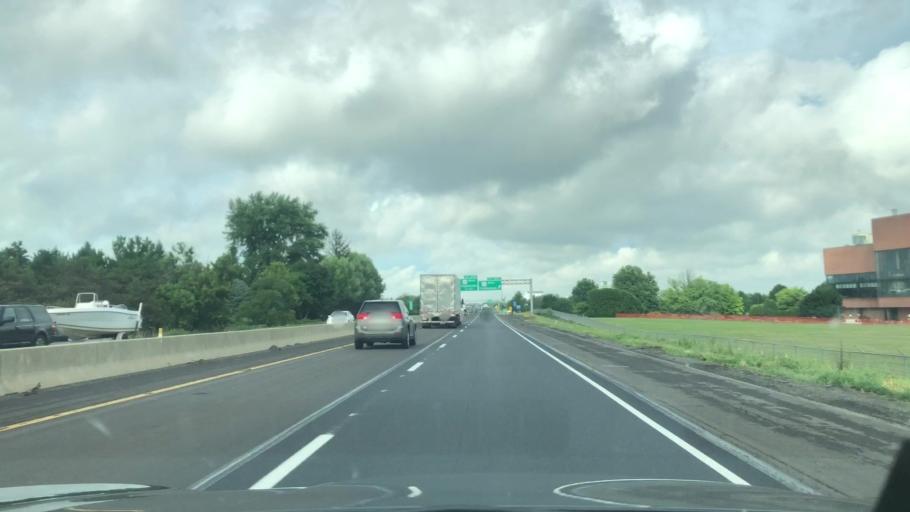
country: US
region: Pennsylvania
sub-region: Lehigh County
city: Trexlertown
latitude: 40.5782
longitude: -75.6333
